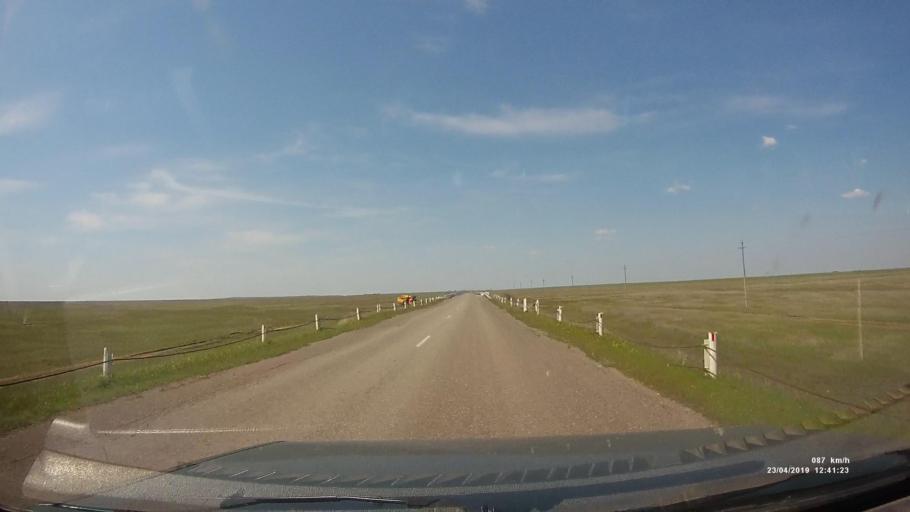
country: RU
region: Kalmykiya
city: Yashalta
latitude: 46.4478
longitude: 42.6818
